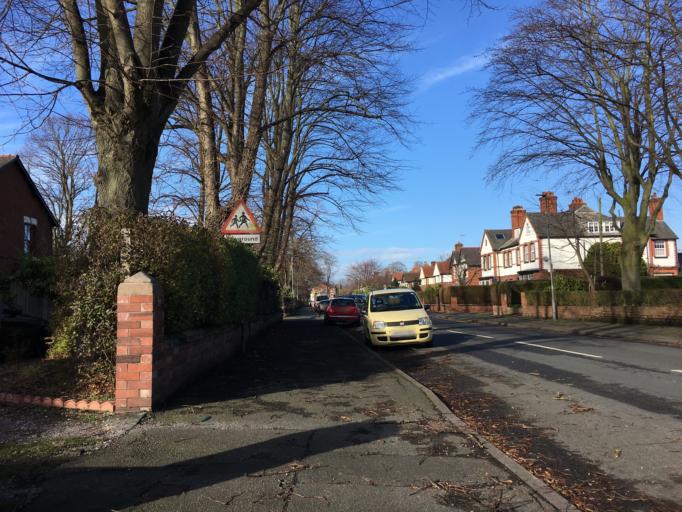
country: GB
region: England
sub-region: Cheshire West and Chester
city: Hoole
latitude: 53.2005
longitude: -2.8679
